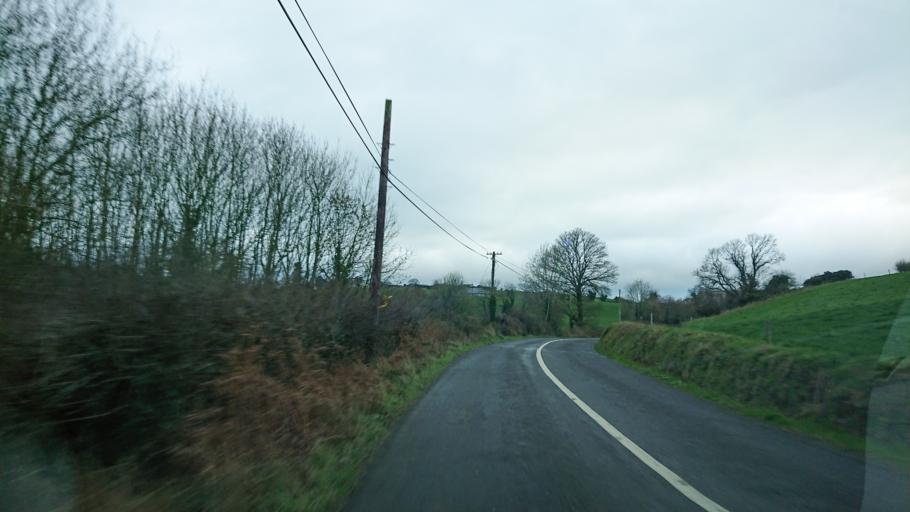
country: IE
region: Munster
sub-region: Waterford
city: Portlaw
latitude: 52.2708
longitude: -7.3925
